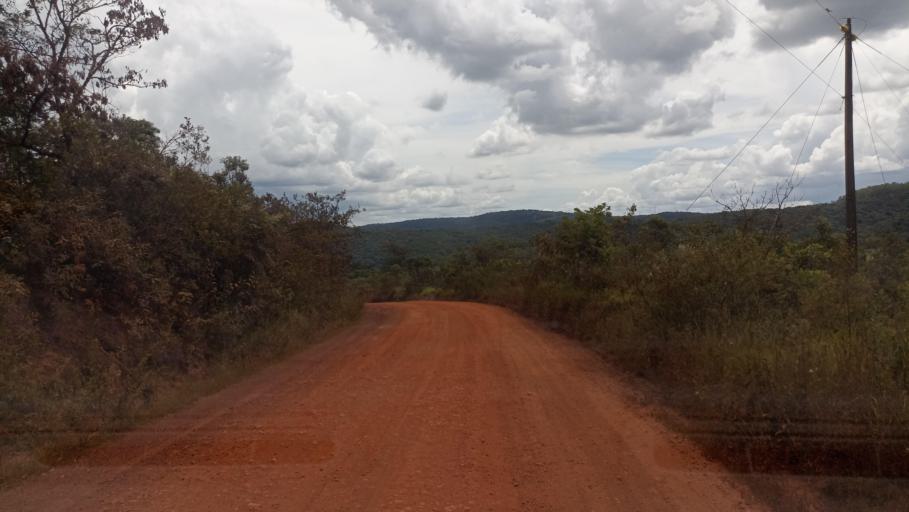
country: BR
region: Minas Gerais
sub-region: Itabirito
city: Itabirito
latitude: -20.3416
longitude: -43.7528
